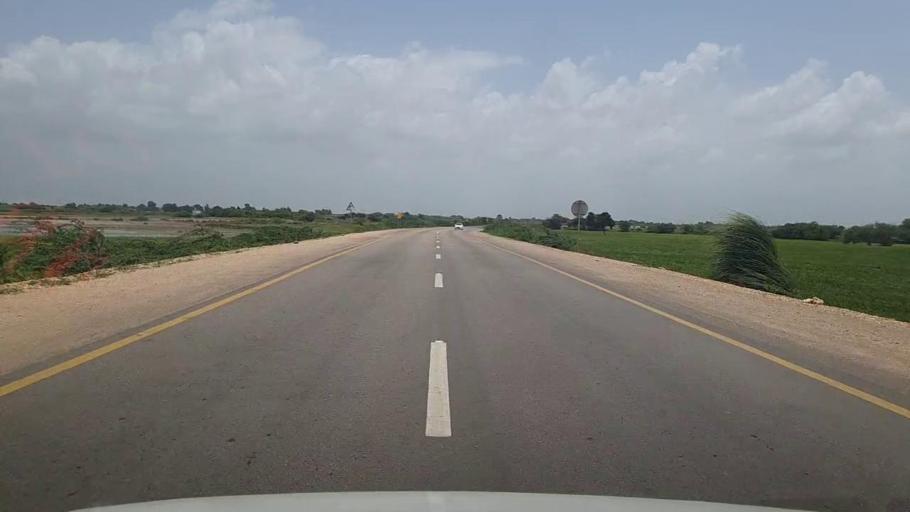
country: PK
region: Sindh
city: Thatta
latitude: 24.7621
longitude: 67.9496
